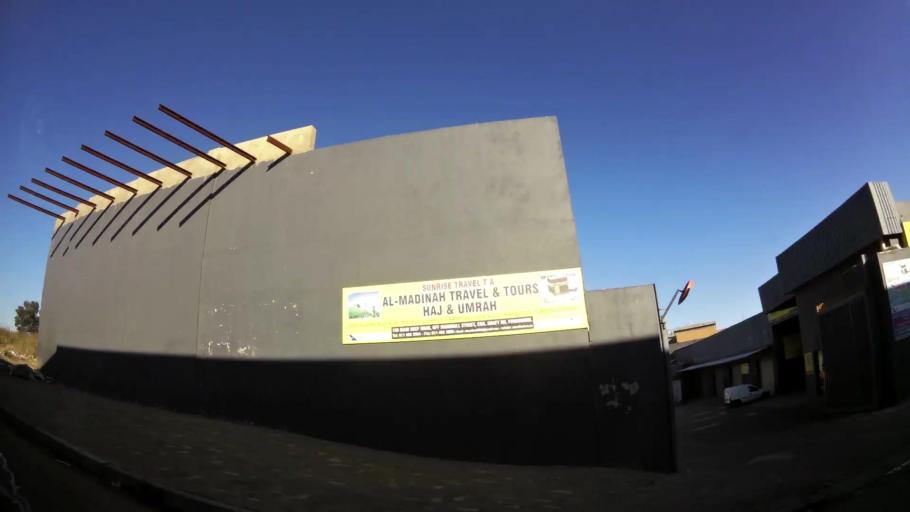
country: ZA
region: Gauteng
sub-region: City of Johannesburg Metropolitan Municipality
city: Johannesburg
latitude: -26.2085
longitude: 28.0286
